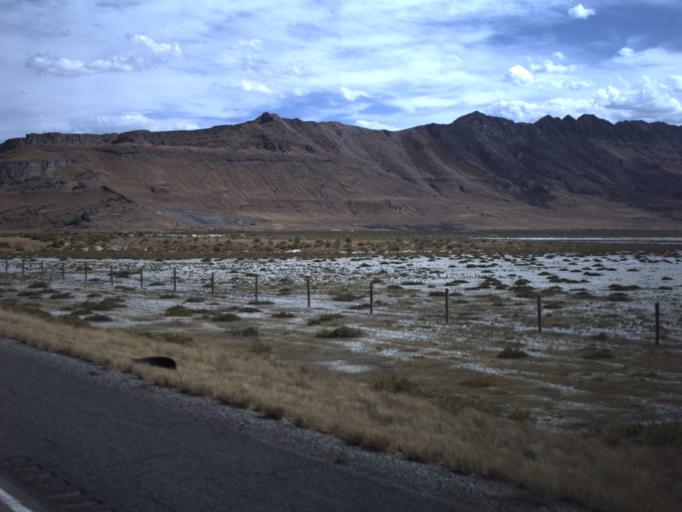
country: US
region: Utah
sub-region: Tooele County
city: Grantsville
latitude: 40.7464
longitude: -112.6612
